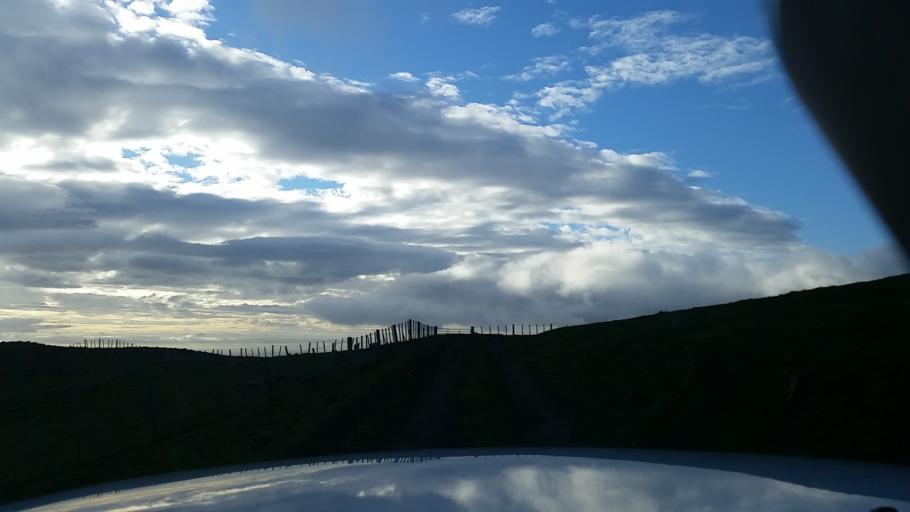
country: NZ
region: Canterbury
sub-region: Christchurch City
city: Christchurch
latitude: -43.6554
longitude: 172.8682
